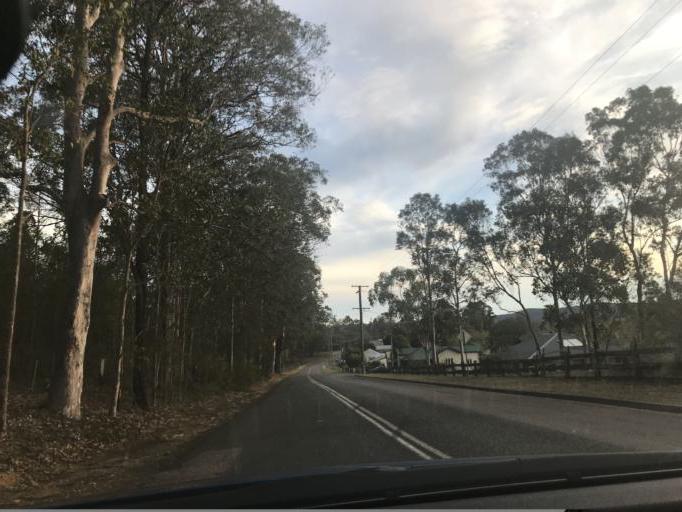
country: AU
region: New South Wales
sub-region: Cessnock
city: Cessnock
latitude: -32.9019
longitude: 151.2917
